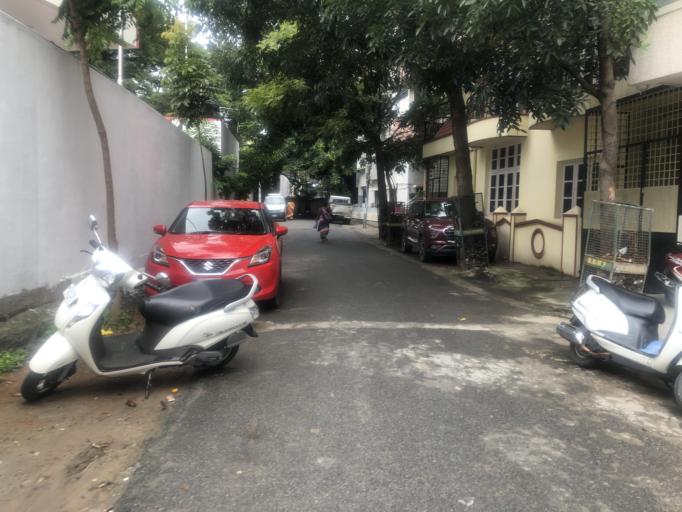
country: IN
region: Karnataka
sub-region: Bangalore Urban
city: Bangalore
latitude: 12.9382
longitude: 77.5489
